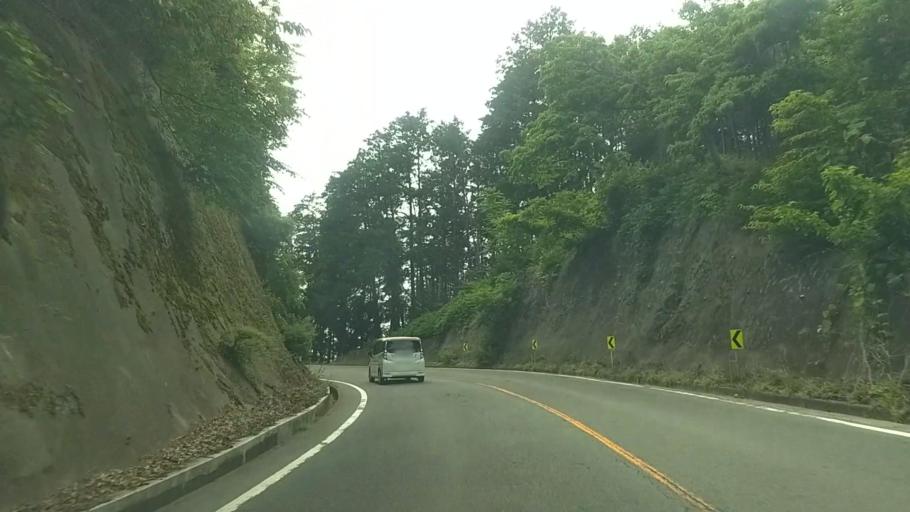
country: JP
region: Yamanashi
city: Isawa
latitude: 35.5684
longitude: 138.5954
